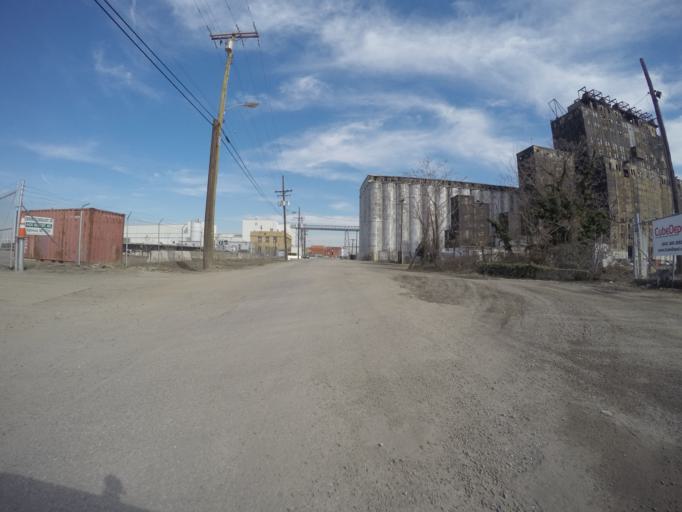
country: US
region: Maryland
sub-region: Baltimore County
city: Dundalk
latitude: 39.2618
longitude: -76.5586
